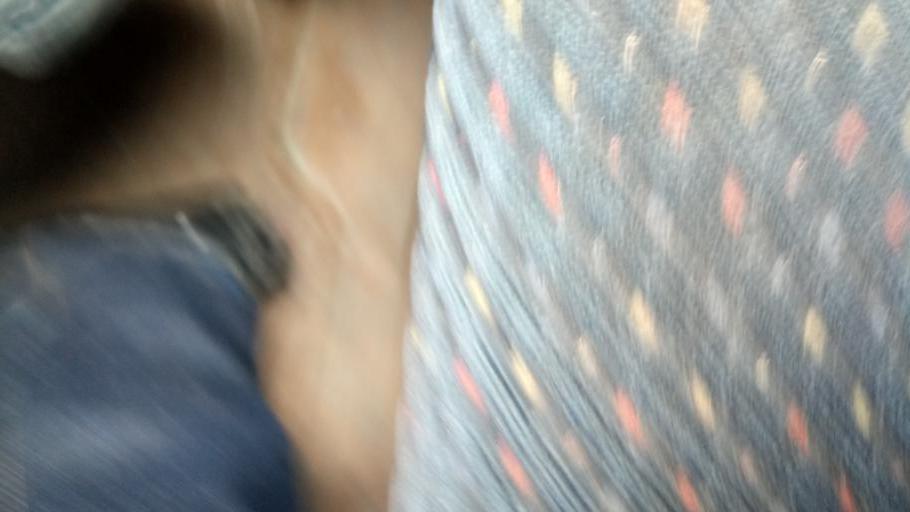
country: CD
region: Katanga
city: Lubumbashi
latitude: -11.6430
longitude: 27.4859
